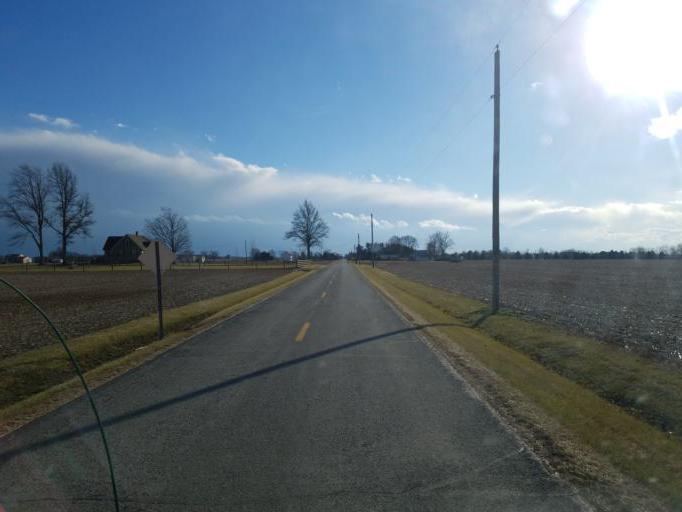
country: US
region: Ohio
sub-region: Marion County
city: Prospect
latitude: 40.4207
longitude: -83.1427
